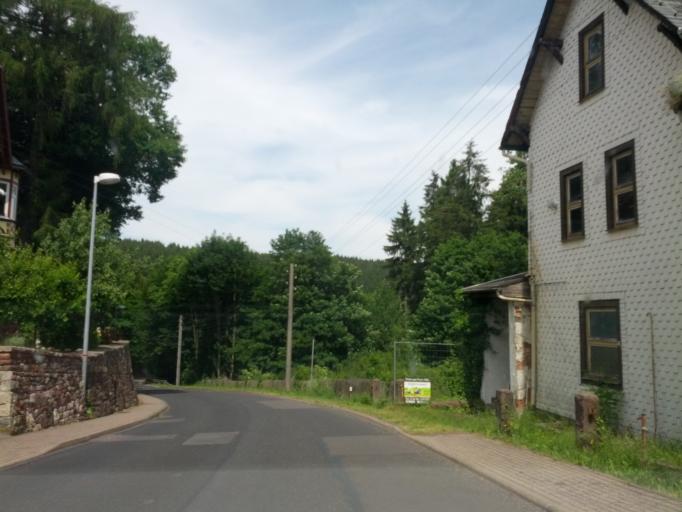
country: DE
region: Thuringia
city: Finsterbergen
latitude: 50.8376
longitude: 10.5961
